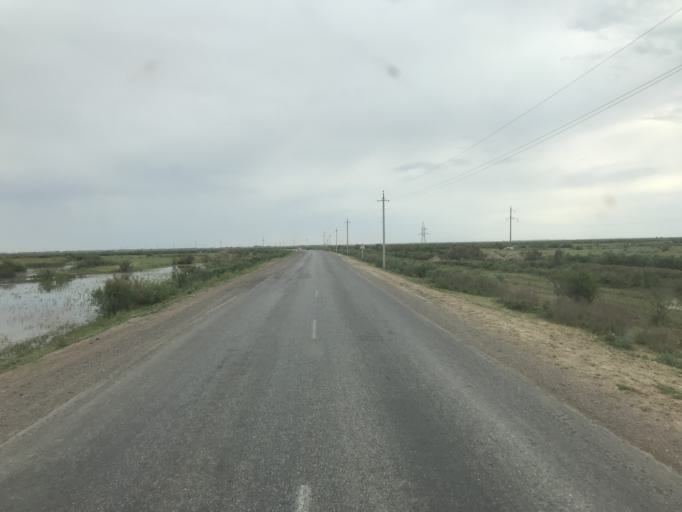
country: KZ
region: Ongtustik Qazaqstan
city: Asykata
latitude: 41.0077
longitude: 68.4775
